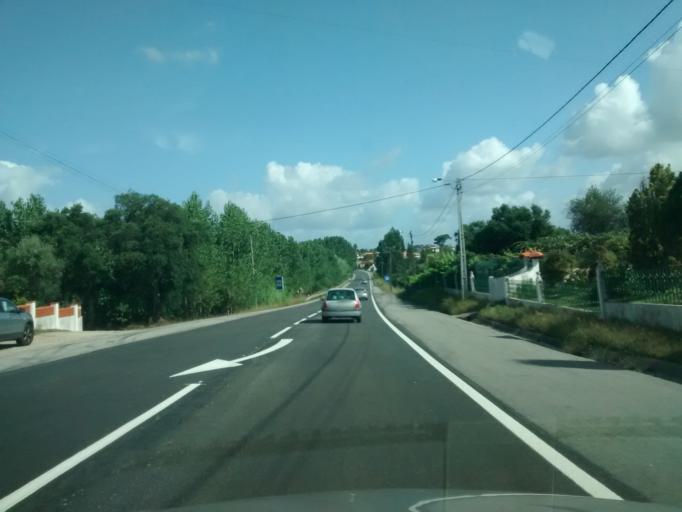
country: PT
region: Aveiro
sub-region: Oliveira do Bairro
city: Oliveira do Bairro
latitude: 40.5277
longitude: -8.5082
